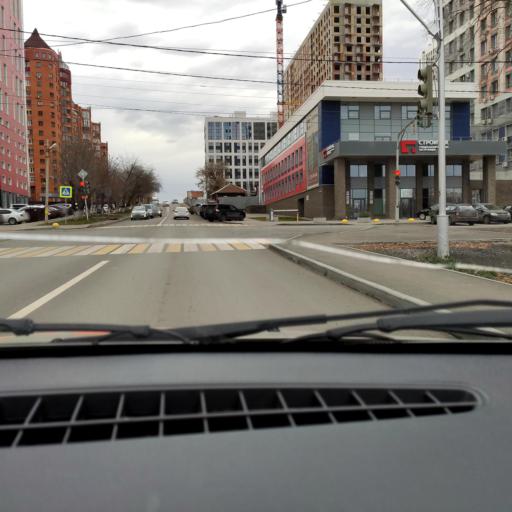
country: RU
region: Bashkortostan
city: Ufa
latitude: 54.7318
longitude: 55.9309
